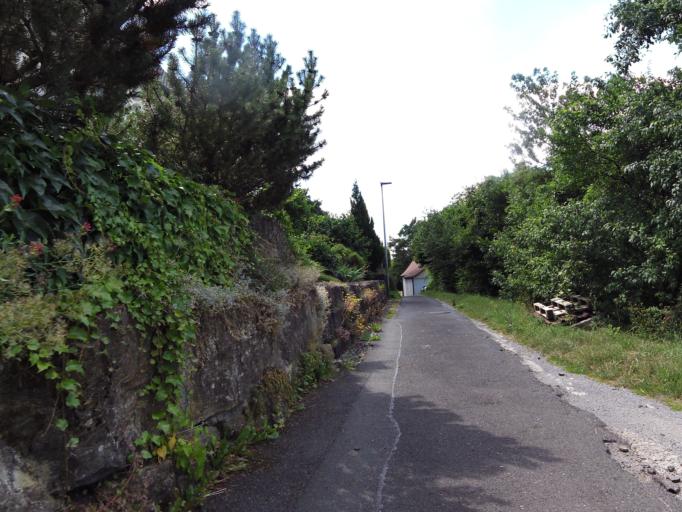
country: DE
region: Bavaria
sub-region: Regierungsbezirk Unterfranken
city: Gadheim
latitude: 49.8240
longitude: 9.9244
